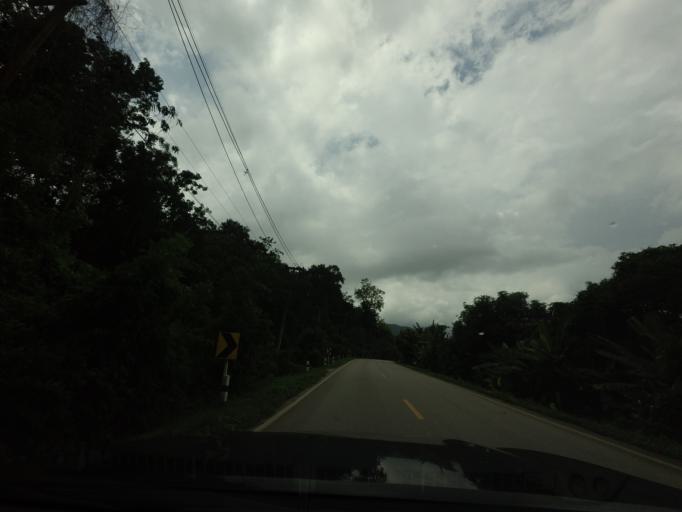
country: TH
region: Loei
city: Pak Chom
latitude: 18.0537
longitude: 101.8129
